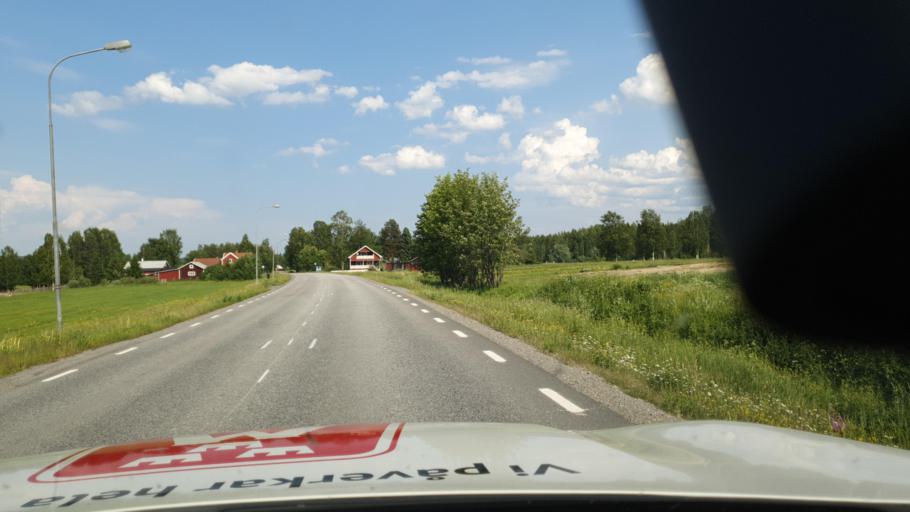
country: SE
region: Vaesterbotten
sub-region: Skelleftea Kommun
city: Viken
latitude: 64.7490
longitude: 20.8719
